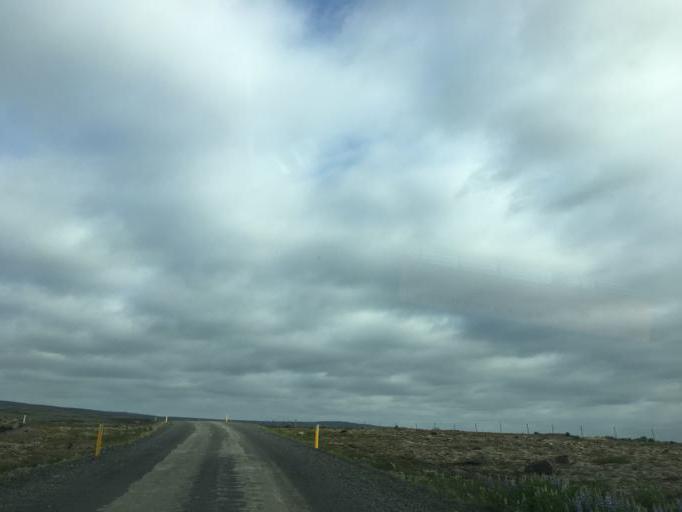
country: IS
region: South
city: Selfoss
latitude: 64.2980
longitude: -20.2421
